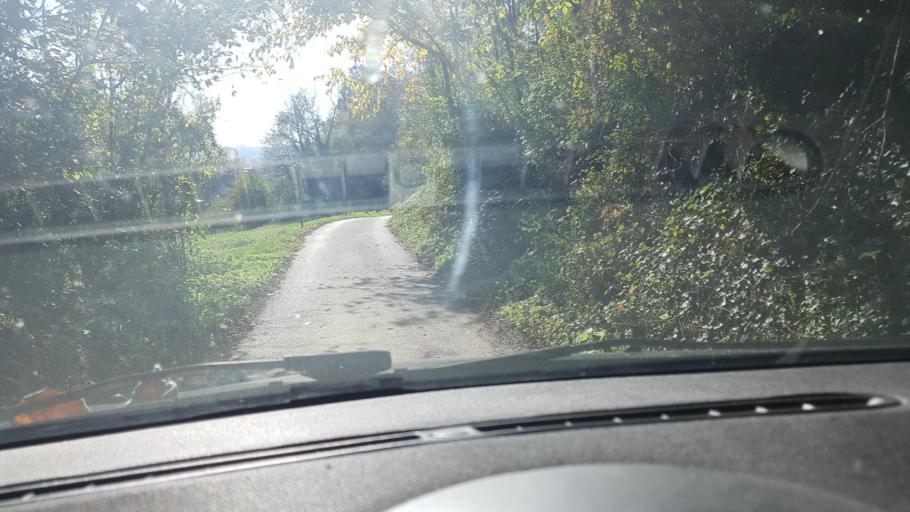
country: HR
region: Krapinsko-Zagorska
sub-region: Grad Krapina
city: Krapina
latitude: 46.1550
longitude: 15.8816
